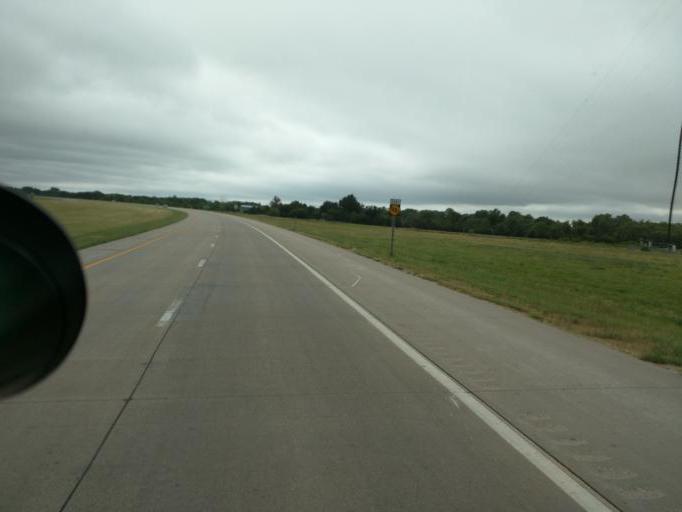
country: US
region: Kansas
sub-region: Reno County
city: South Hutchinson
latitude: 37.9727
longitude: -97.9380
